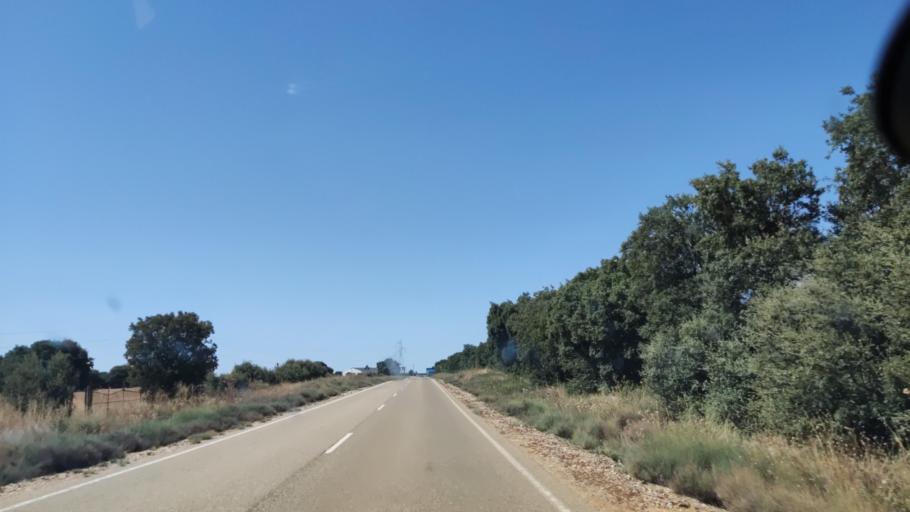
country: ES
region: Castille and Leon
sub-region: Provincia de Valladolid
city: Uruena
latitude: 41.6992
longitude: -5.2116
